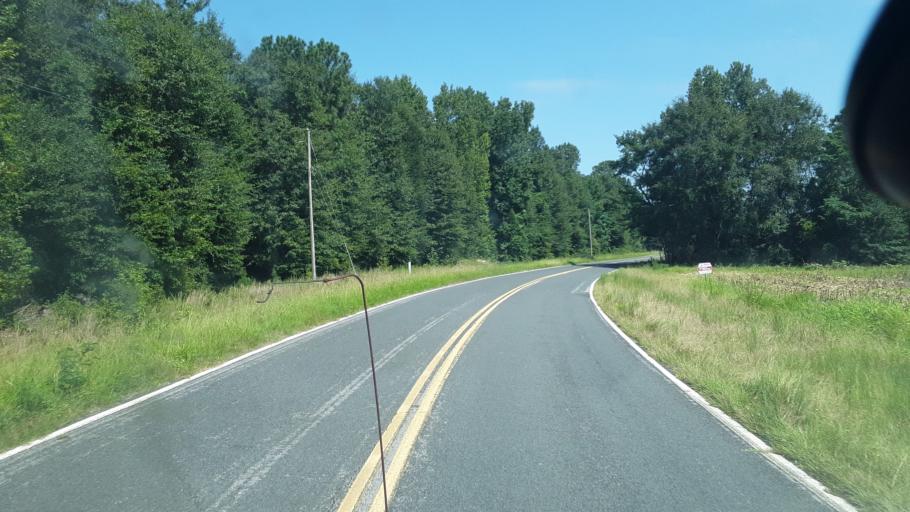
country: US
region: South Carolina
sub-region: Bamberg County
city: Bamberg
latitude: 33.3720
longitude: -81.0142
